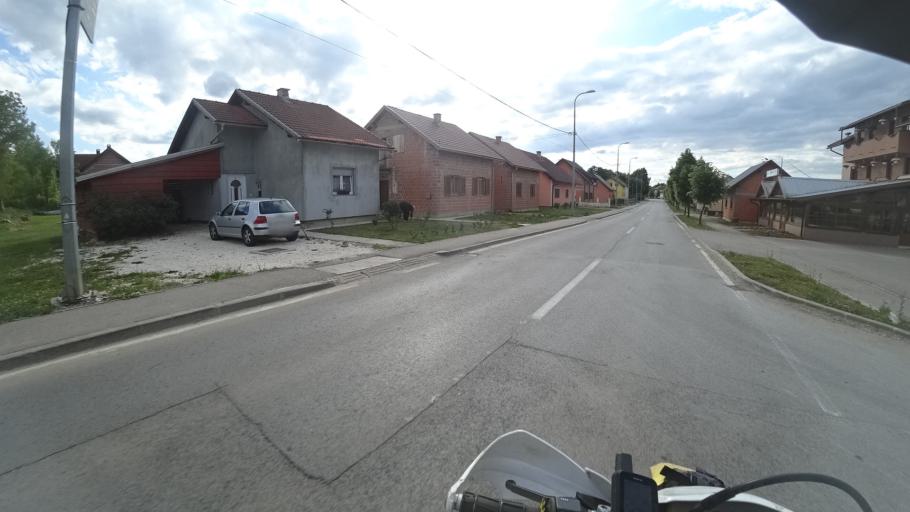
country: HR
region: Licko-Senjska
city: Gospic
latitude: 44.5390
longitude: 15.3852
